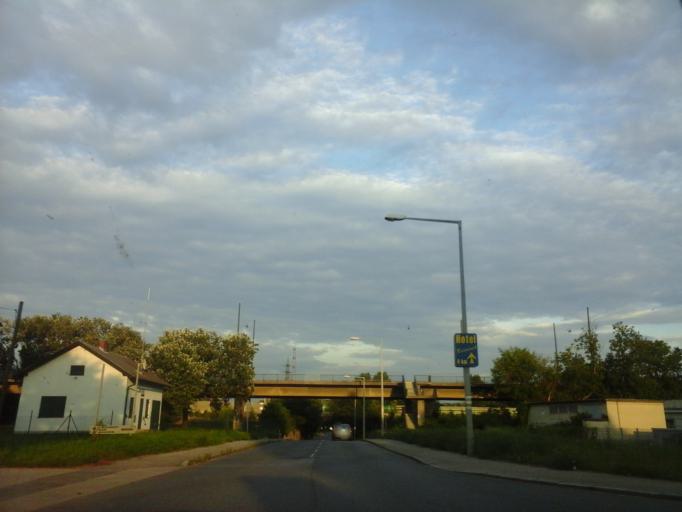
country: AT
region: Lower Austria
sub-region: Politischer Bezirk Wien-Umgebung
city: Schwechat
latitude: 48.1704
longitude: 16.4768
